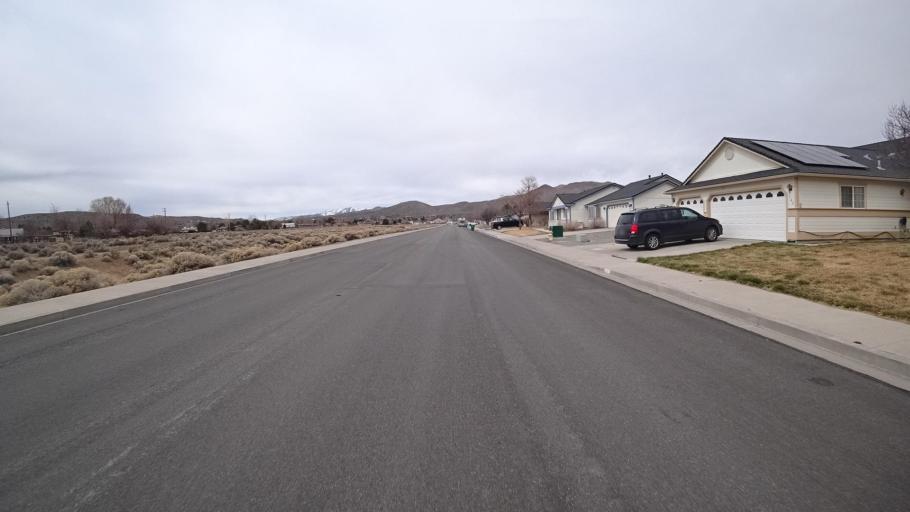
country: US
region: Nevada
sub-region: Washoe County
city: Spanish Springs
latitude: 39.6365
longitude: -119.7213
